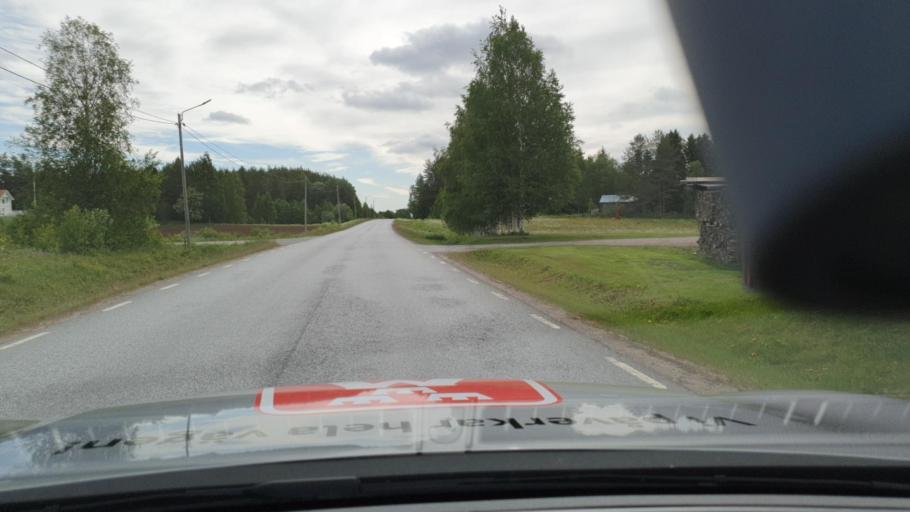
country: SE
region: Norrbotten
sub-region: Kalix Kommun
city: Rolfs
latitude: 65.8872
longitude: 22.9701
